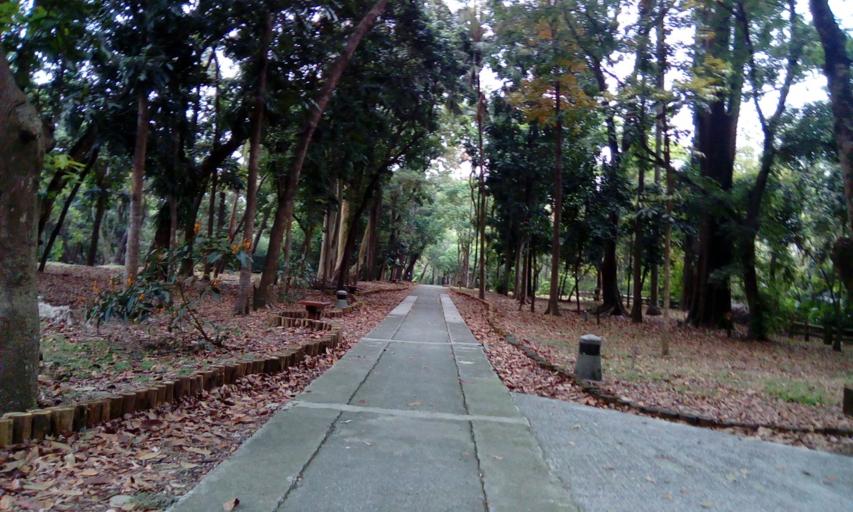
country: TW
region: Taiwan
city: Lugu
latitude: 23.7758
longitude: 120.6728
